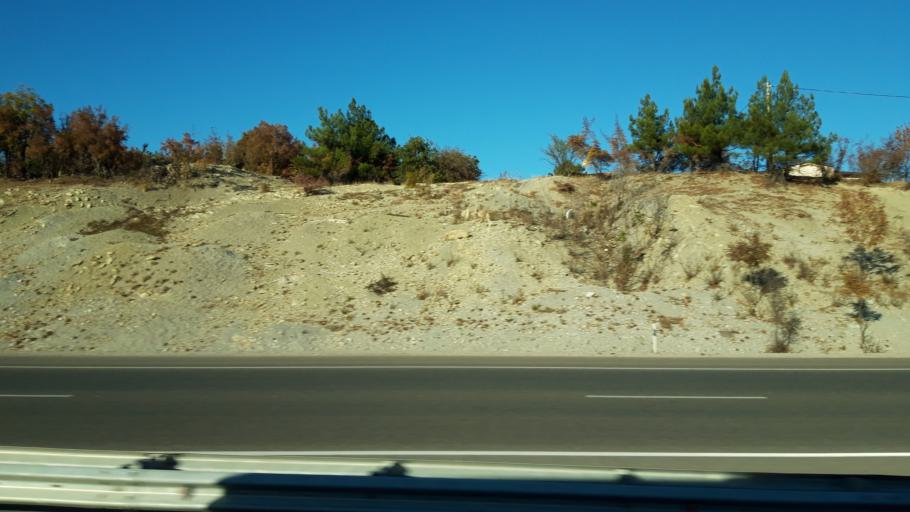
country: RU
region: Krasnodarskiy
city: Kabardinka
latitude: 44.6396
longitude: 37.9846
